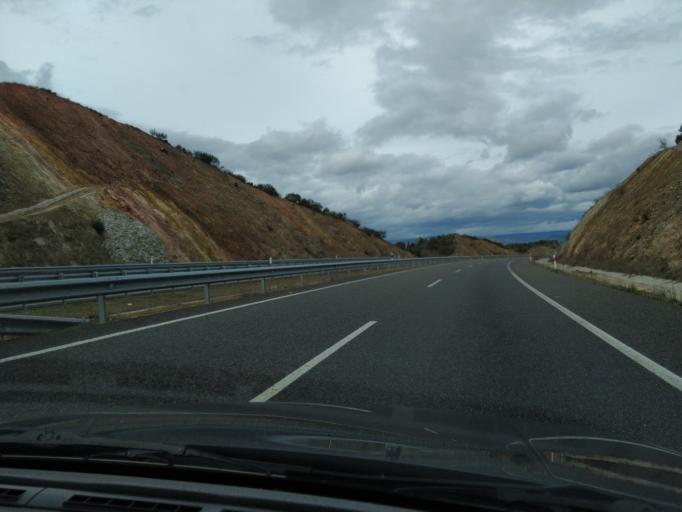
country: ES
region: Galicia
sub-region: Provincia de Ourense
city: Oimbra
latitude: 41.8563
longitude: -7.4230
